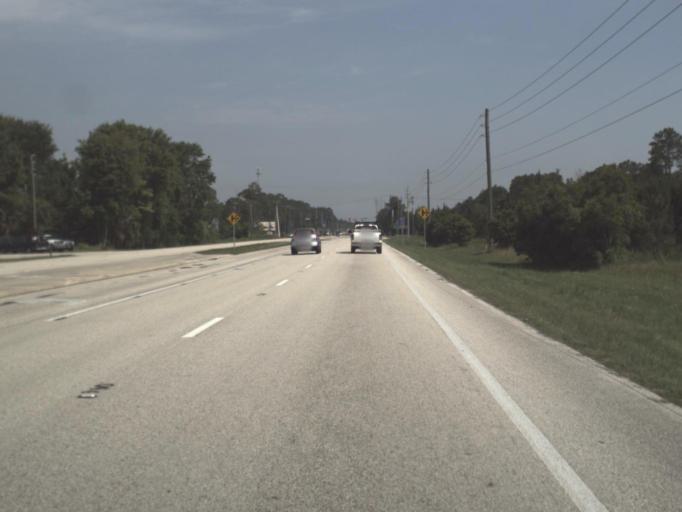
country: US
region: Florida
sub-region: Saint Johns County
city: Palm Valley
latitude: 30.0834
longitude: -81.4574
